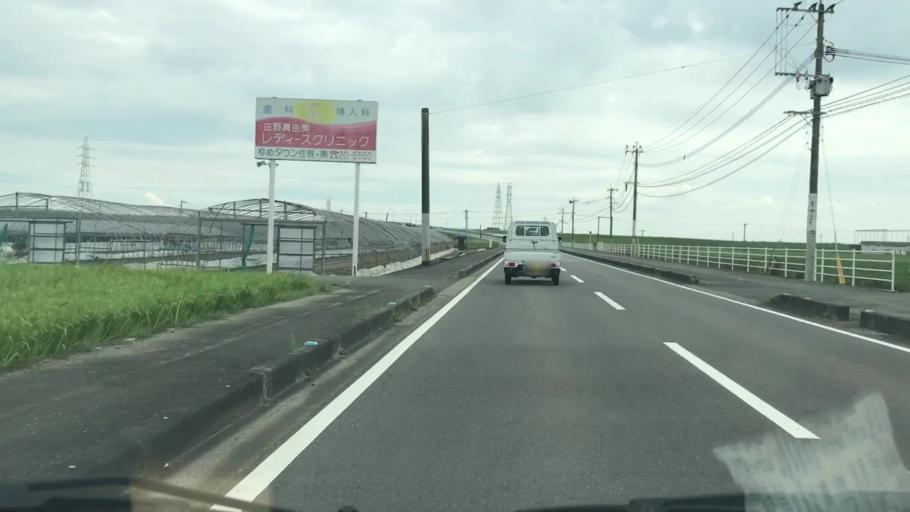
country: JP
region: Saga Prefecture
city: Saga-shi
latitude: 33.2830
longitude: 130.2520
